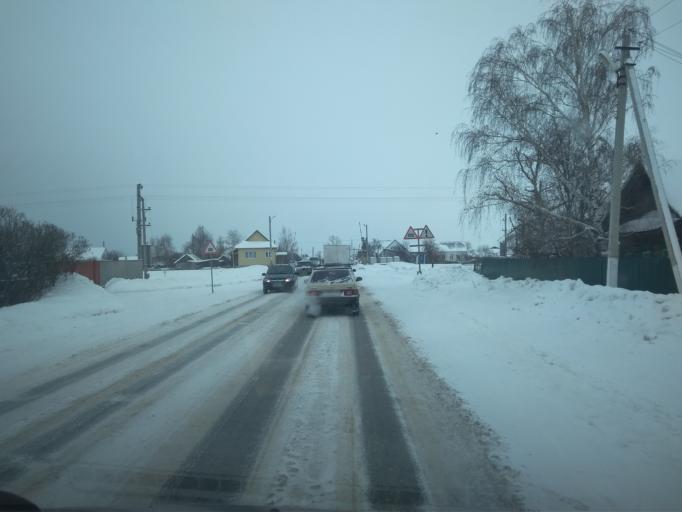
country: RU
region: Mordoviya
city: Kemlya
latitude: 54.6893
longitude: 45.2752
